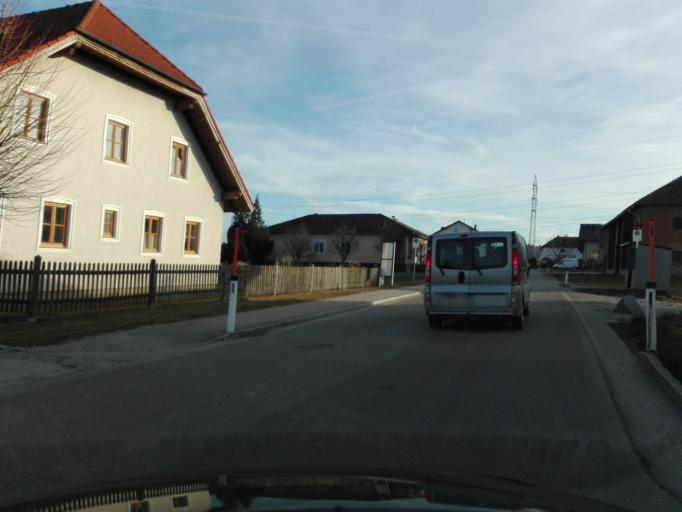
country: AT
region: Lower Austria
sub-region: Politischer Bezirk Amstetten
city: Sankt Valentin
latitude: 48.1292
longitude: 14.5156
